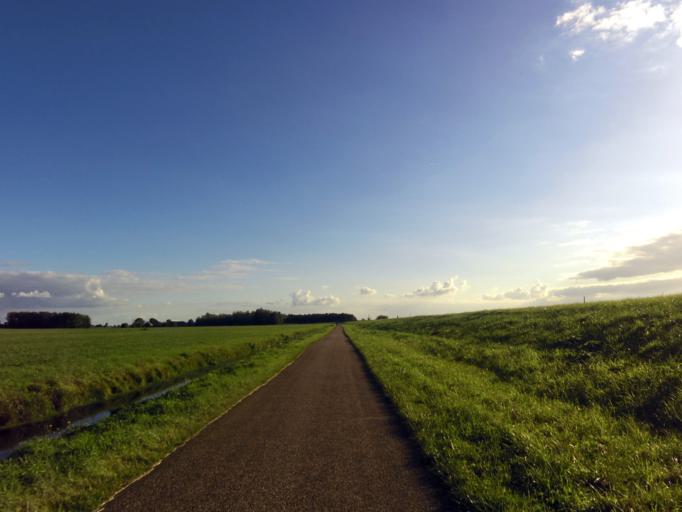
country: NL
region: South Holland
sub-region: Gemeente Alphen aan den Rijn
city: Alphen aan den Rijn
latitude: 52.1208
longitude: 4.6039
